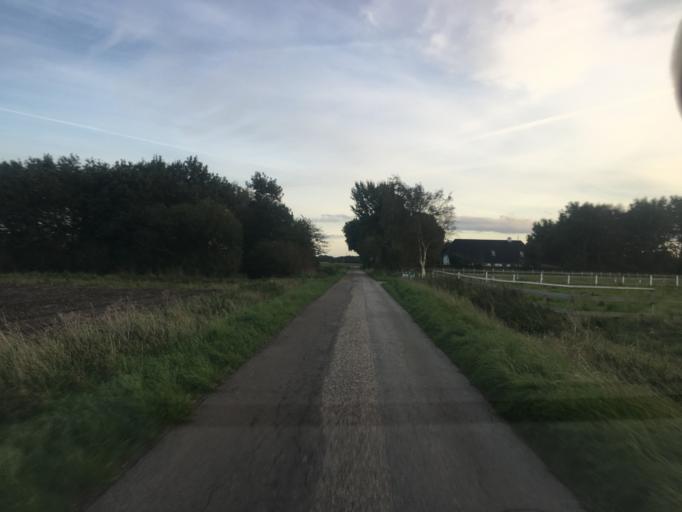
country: DK
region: South Denmark
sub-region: Tonder Kommune
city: Tonder
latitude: 54.9725
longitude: 8.9042
